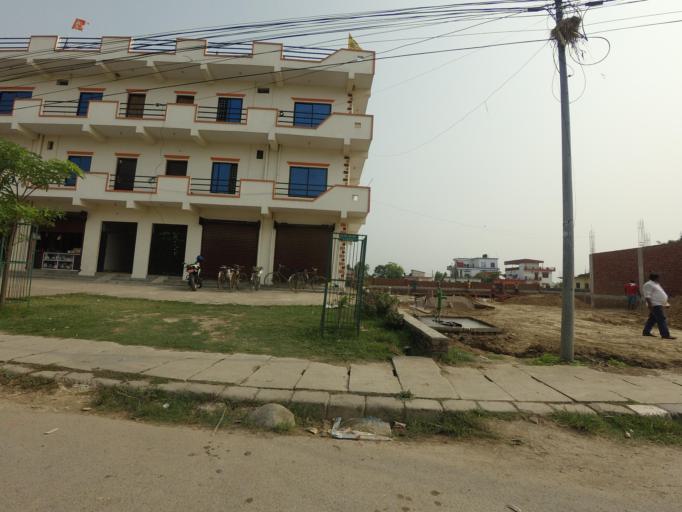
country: NP
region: Western Region
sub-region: Lumbini Zone
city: Bhairahawa
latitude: 27.5174
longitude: 83.4639
